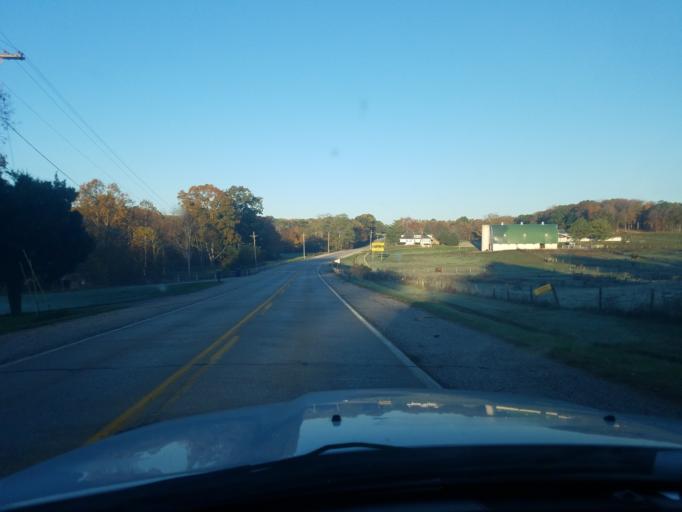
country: US
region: Indiana
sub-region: Floyd County
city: Galena
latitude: 38.3824
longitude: -86.0221
